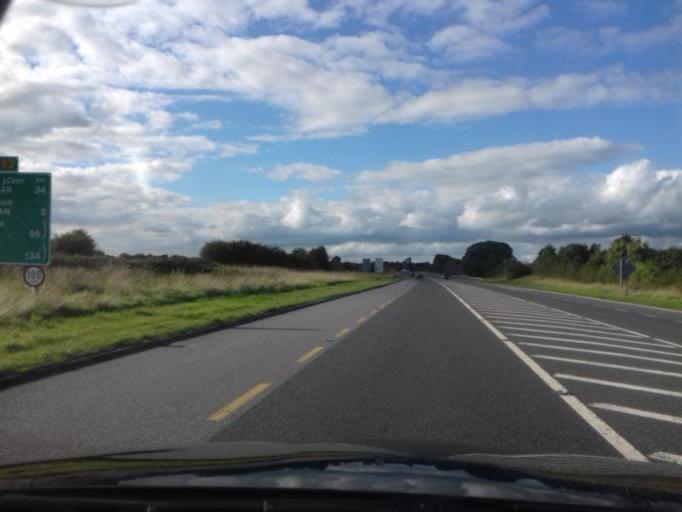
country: IE
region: Leinster
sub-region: Uibh Fhaili
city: Tullamore
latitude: 53.3045
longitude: -7.4915
